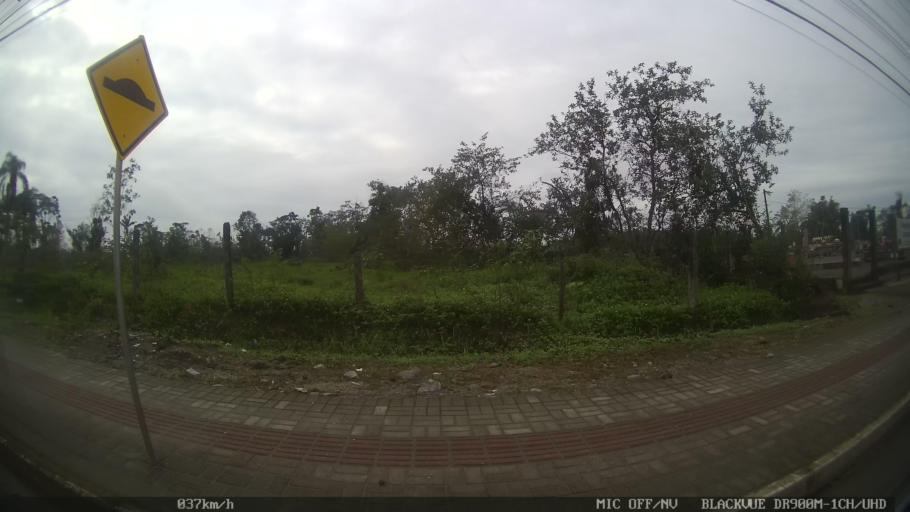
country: BR
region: Santa Catarina
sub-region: Joinville
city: Joinville
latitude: -26.0447
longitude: -48.8558
